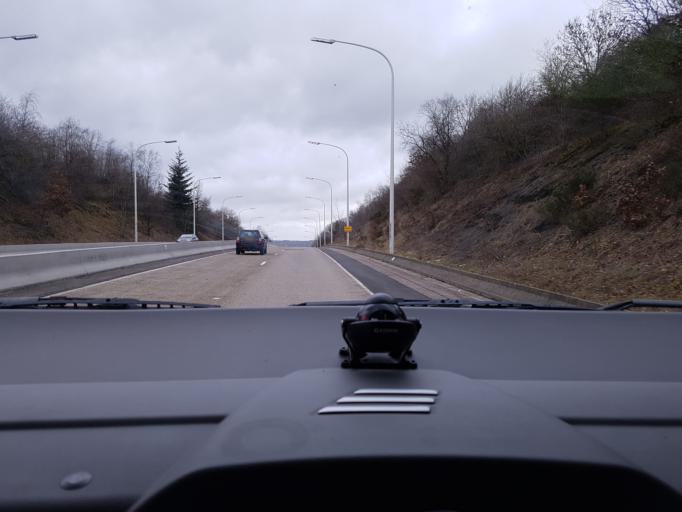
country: BE
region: Wallonia
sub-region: Province du Luxembourg
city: Marche-en-Famenne
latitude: 50.2582
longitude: 5.2653
